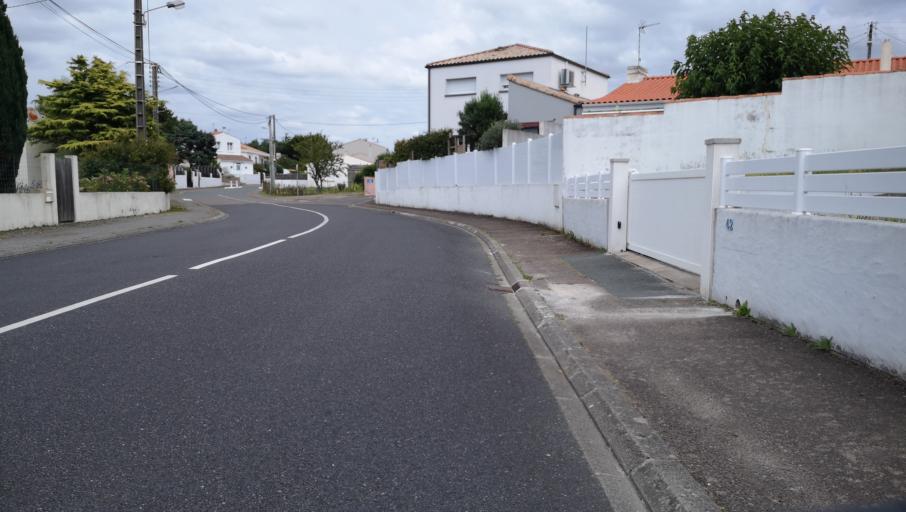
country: FR
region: Pays de la Loire
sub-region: Departement de la Vendee
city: Les Sables-d'Olonne
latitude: 46.5039
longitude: -1.7683
